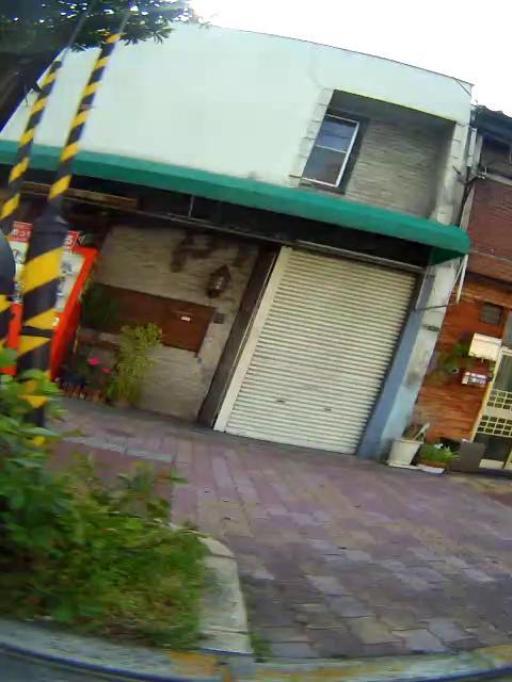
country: JP
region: Osaka
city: Moriguchi
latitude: 34.6998
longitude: 135.5462
